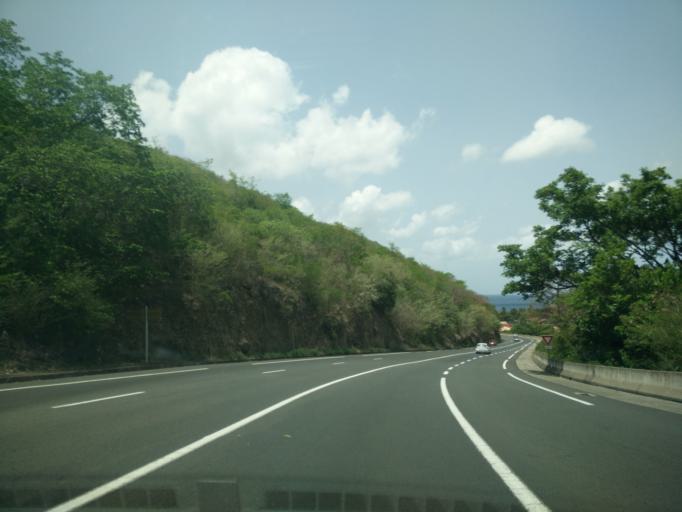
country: MQ
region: Martinique
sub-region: Martinique
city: Saint-Pierre
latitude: 14.6618
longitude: -61.1537
